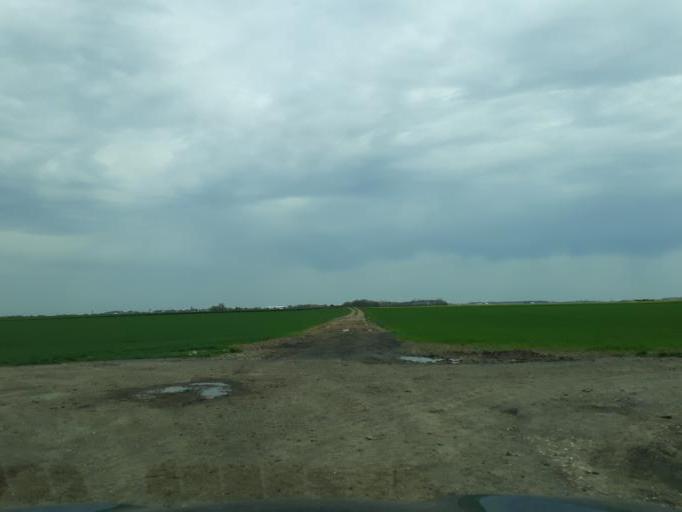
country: FR
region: Centre
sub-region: Departement du Loiret
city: Epieds-en-Beauce
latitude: 47.9603
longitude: 1.6508
